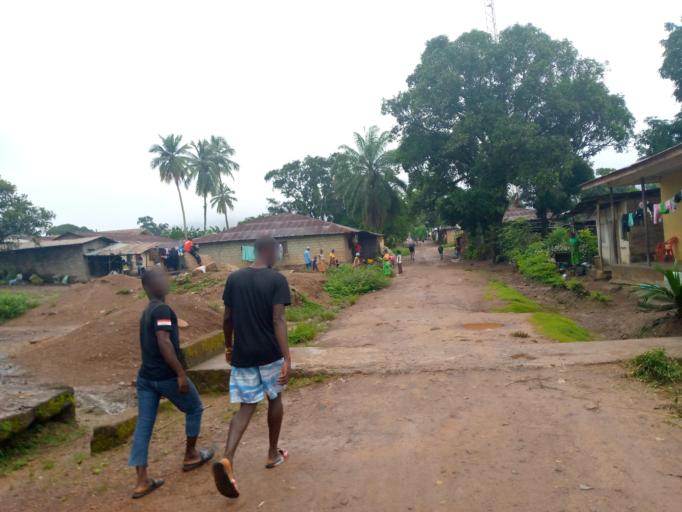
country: SL
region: Eastern Province
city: Kenema
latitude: 7.8814
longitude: -11.1812
